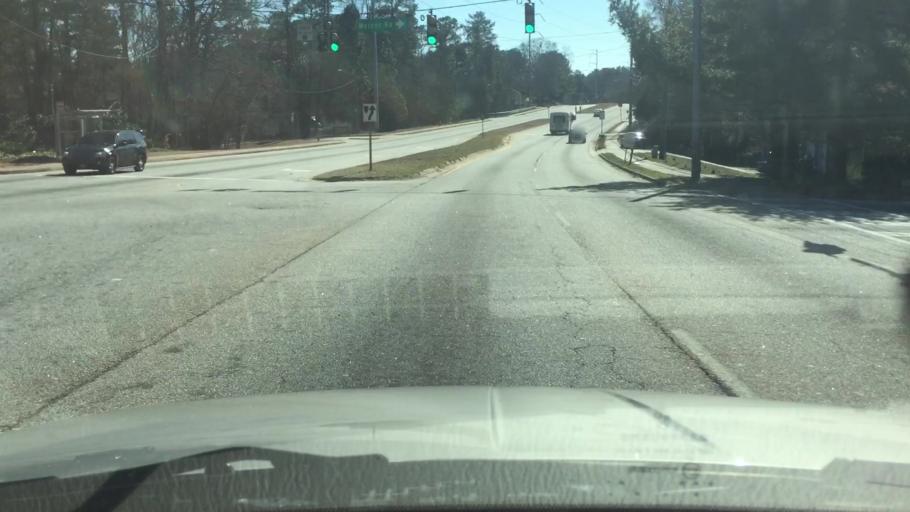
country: US
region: Georgia
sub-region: DeKalb County
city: Stone Mountain
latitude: 33.7531
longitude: -84.1972
